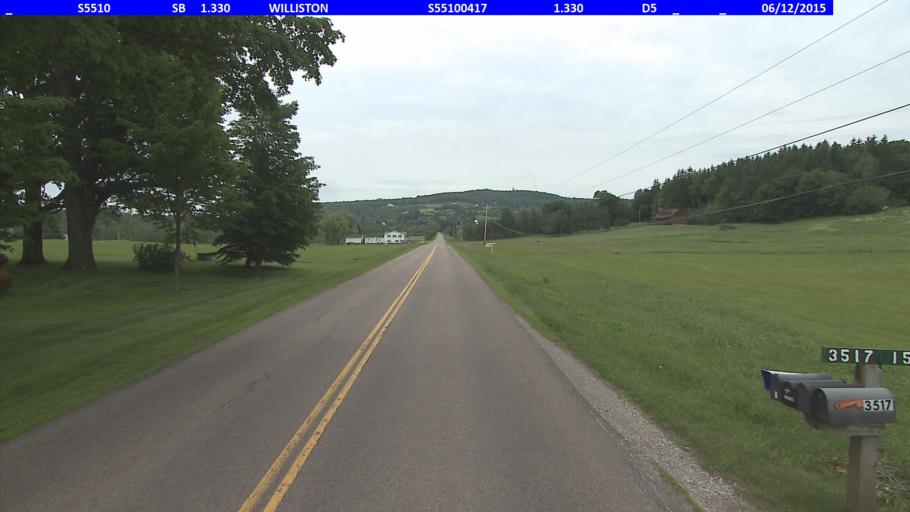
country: US
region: Vermont
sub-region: Chittenden County
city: Williston
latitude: 44.3913
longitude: -73.0949
